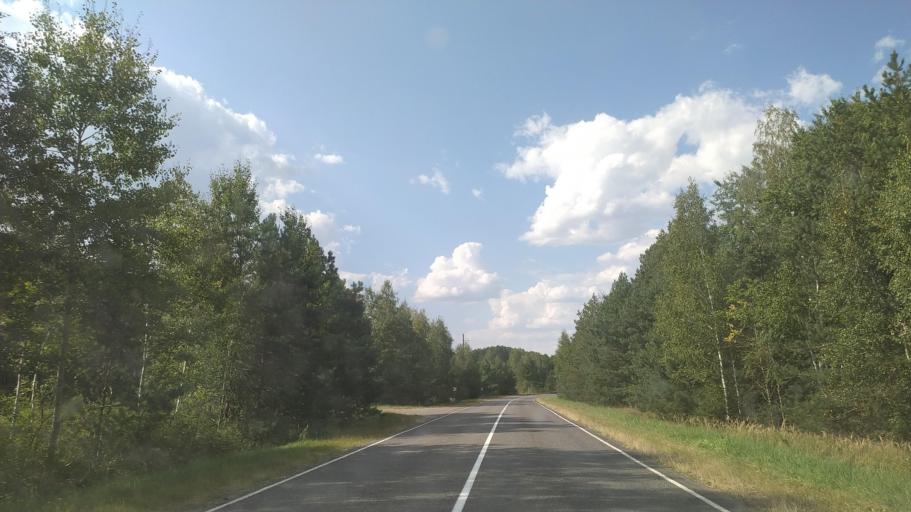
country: BY
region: Brest
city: Drahichyn
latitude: 52.2274
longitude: 25.1168
